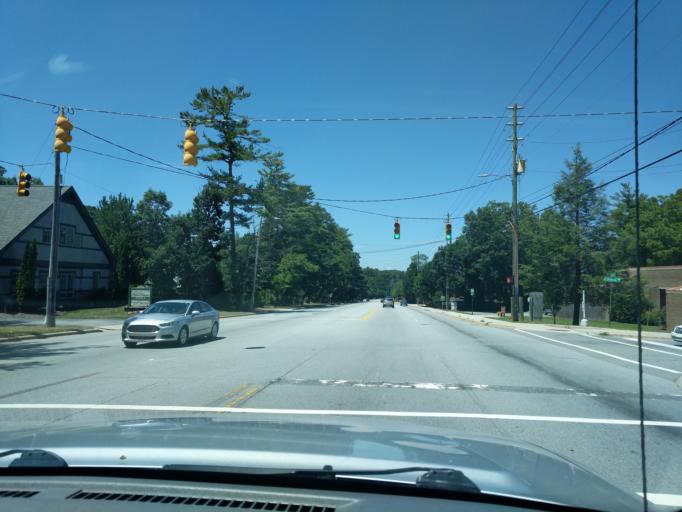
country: US
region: North Carolina
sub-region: Buncombe County
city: Biltmore Forest
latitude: 35.5363
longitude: -82.5289
